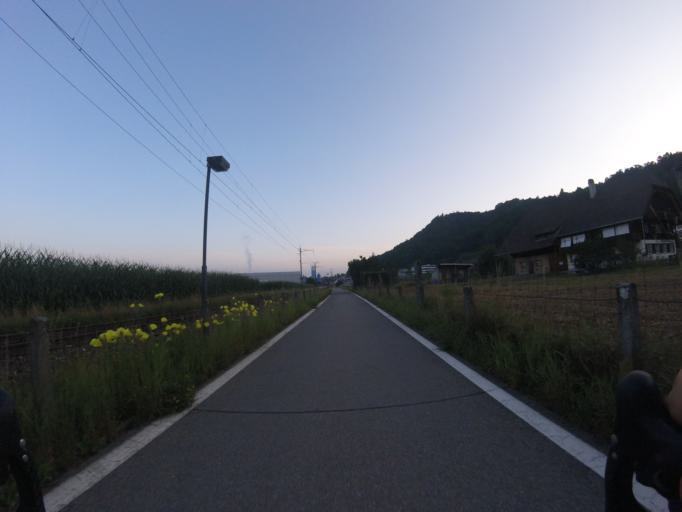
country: CH
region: Bern
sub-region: Thun District
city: Heimberg
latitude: 46.7864
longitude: 7.6077
